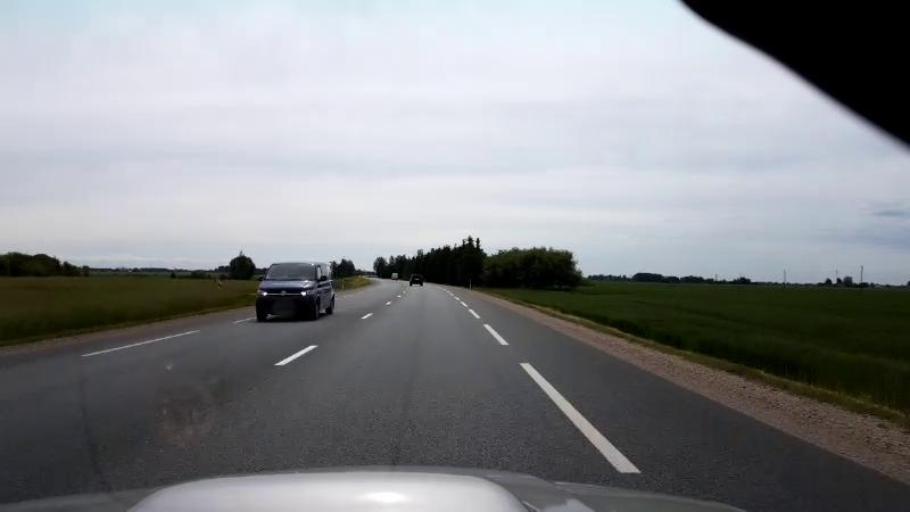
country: LV
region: Bauskas Rajons
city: Bauska
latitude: 56.4419
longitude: 24.1690
